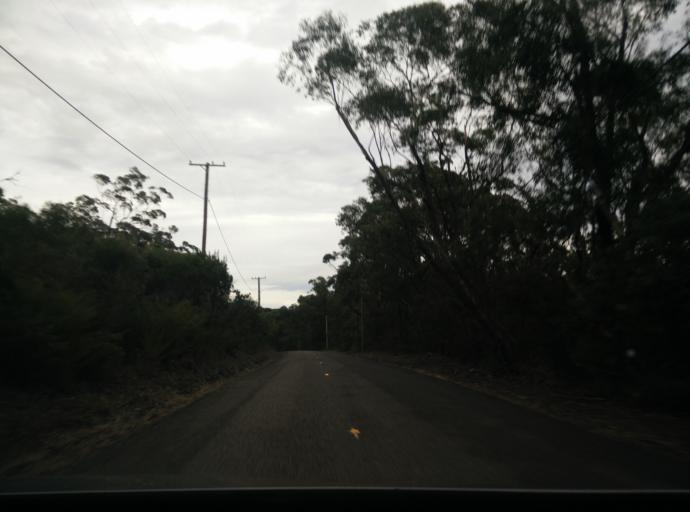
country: AU
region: New South Wales
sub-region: Gosford Shire
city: Narara
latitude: -33.3549
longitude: 151.2987
